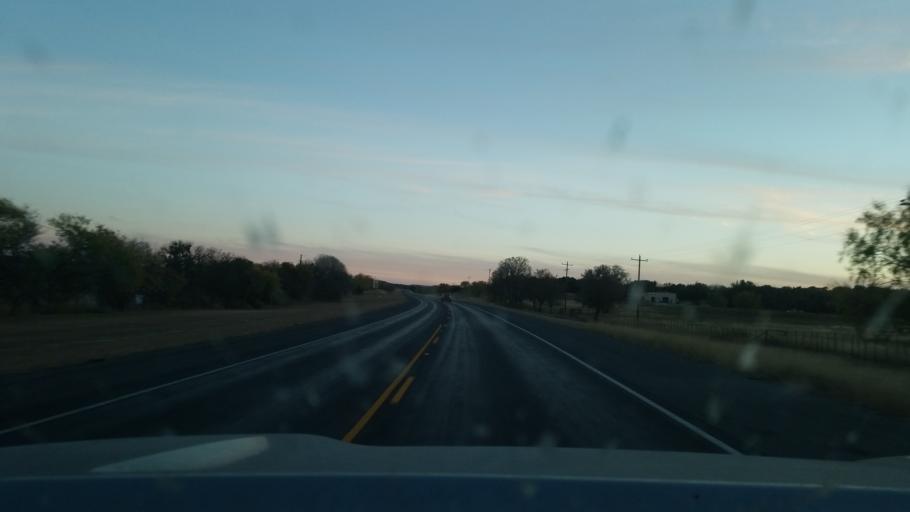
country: US
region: Texas
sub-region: Stephens County
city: Breckenridge
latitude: 32.5978
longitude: -98.8994
